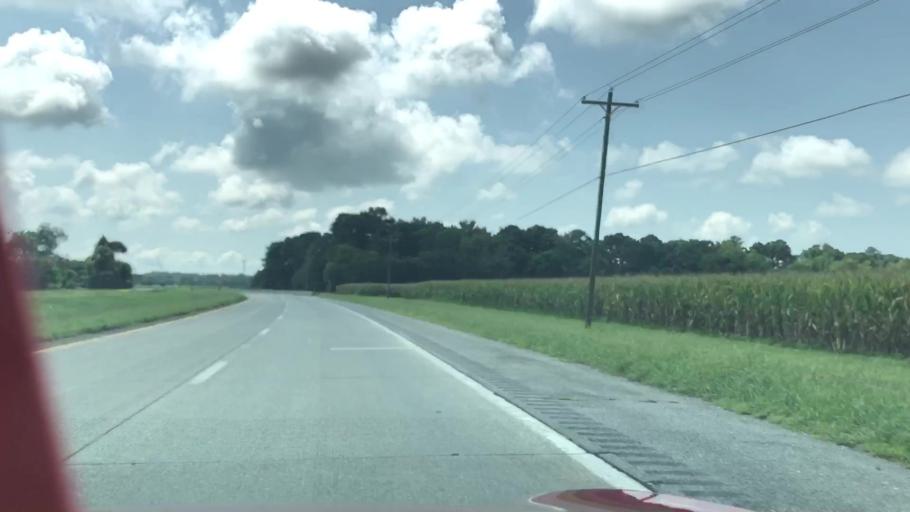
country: US
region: Virginia
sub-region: Northampton County
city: Cape Charles
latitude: 37.2844
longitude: -75.9799
